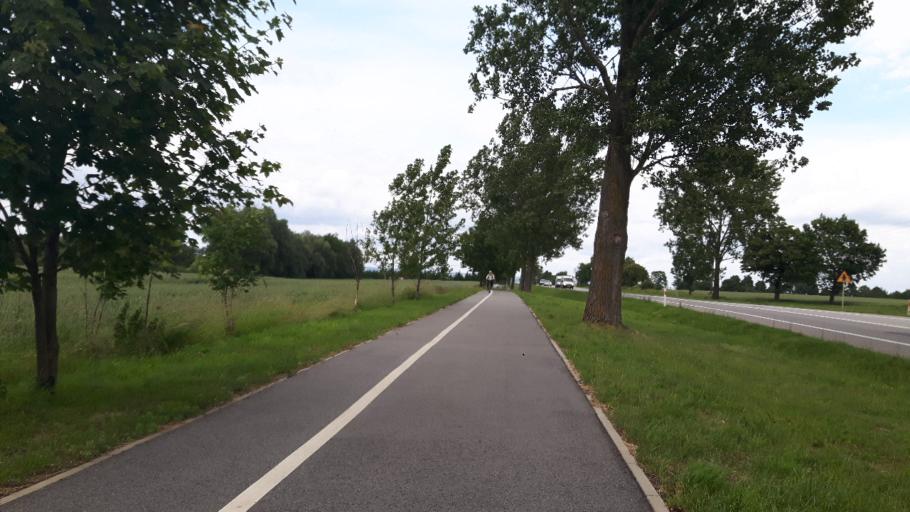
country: PL
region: West Pomeranian Voivodeship
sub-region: Powiat policki
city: Kolbaskowo
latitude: 53.3510
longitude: 14.4591
